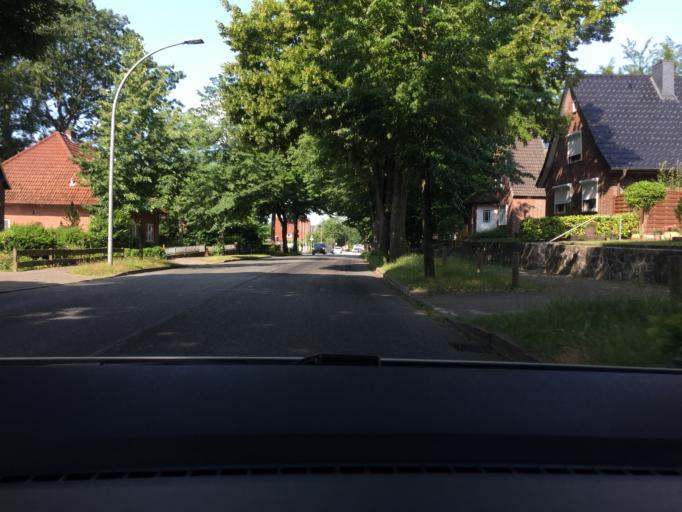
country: DE
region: Schleswig-Holstein
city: Itzehoe
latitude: 53.9305
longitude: 9.5341
